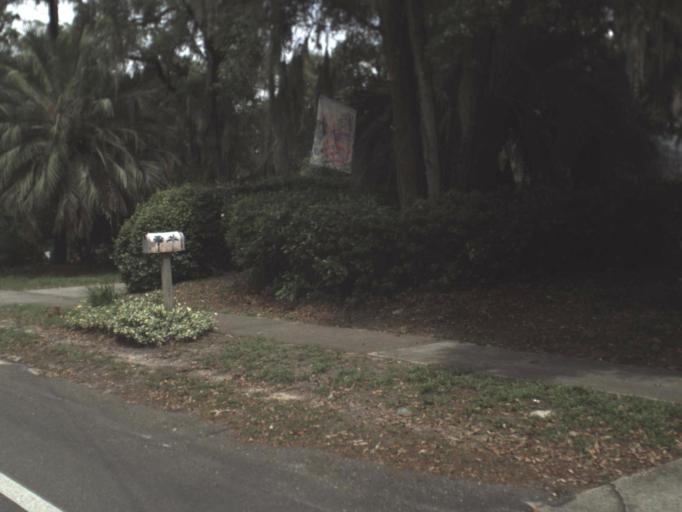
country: US
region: Florida
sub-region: Clay County
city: Keystone Heights
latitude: 29.7790
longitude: -82.0317
